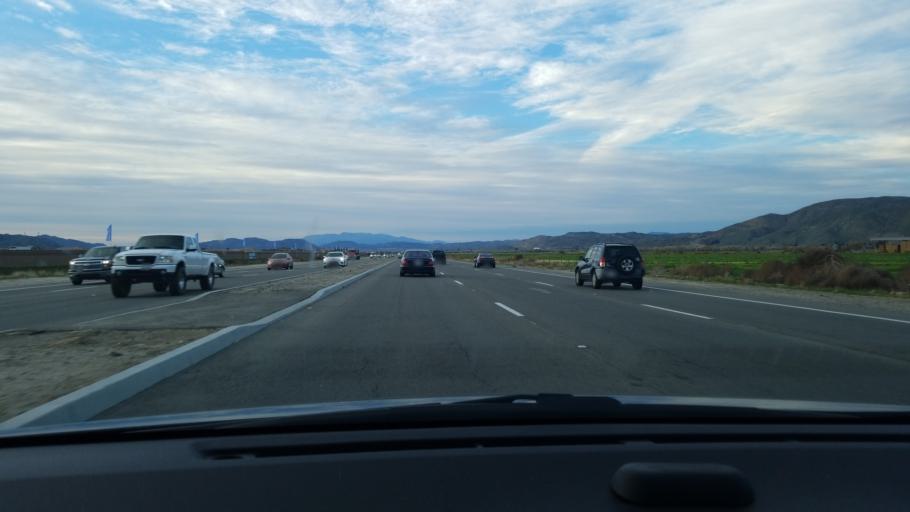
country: US
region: California
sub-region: Riverside County
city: San Jacinto
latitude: 33.8131
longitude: -116.9879
